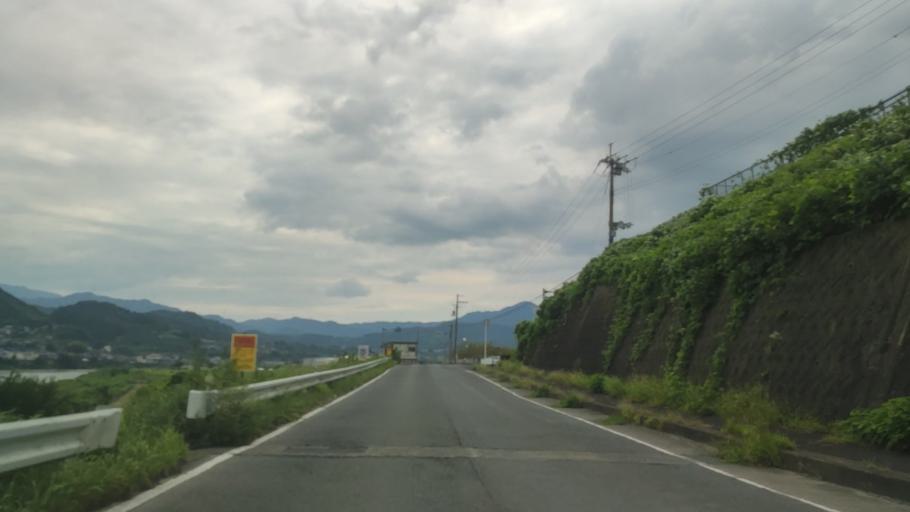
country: JP
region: Wakayama
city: Hashimoto
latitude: 34.3060
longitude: 135.5843
